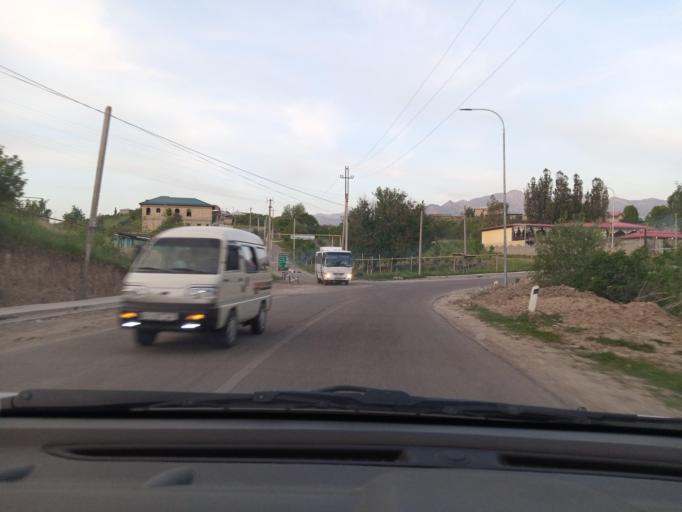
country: UZ
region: Toshkent
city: Parkent
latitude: 41.2463
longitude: 69.7404
